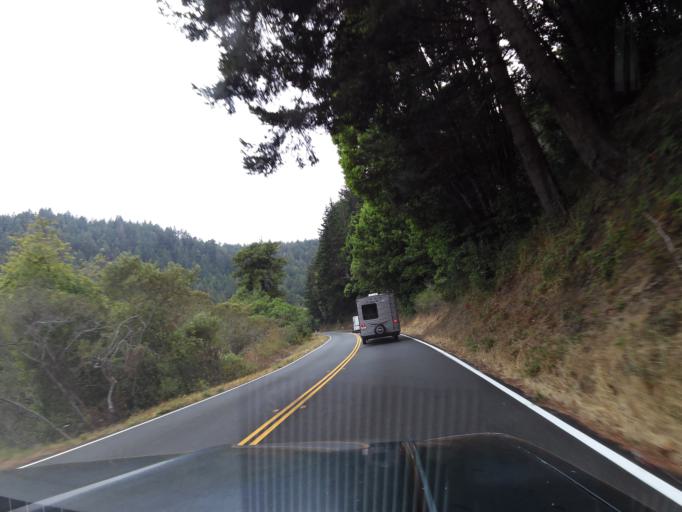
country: US
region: California
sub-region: Mendocino County
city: Fort Bragg
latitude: 39.1890
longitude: -123.7238
